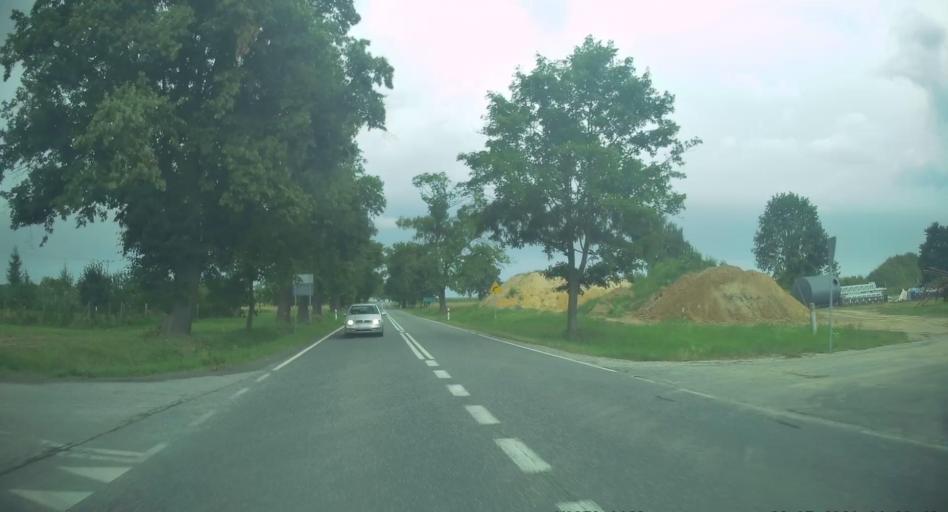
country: PL
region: Lodz Voivodeship
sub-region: Powiat skierniewicki
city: Gluchow
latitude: 51.7789
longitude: 20.0850
